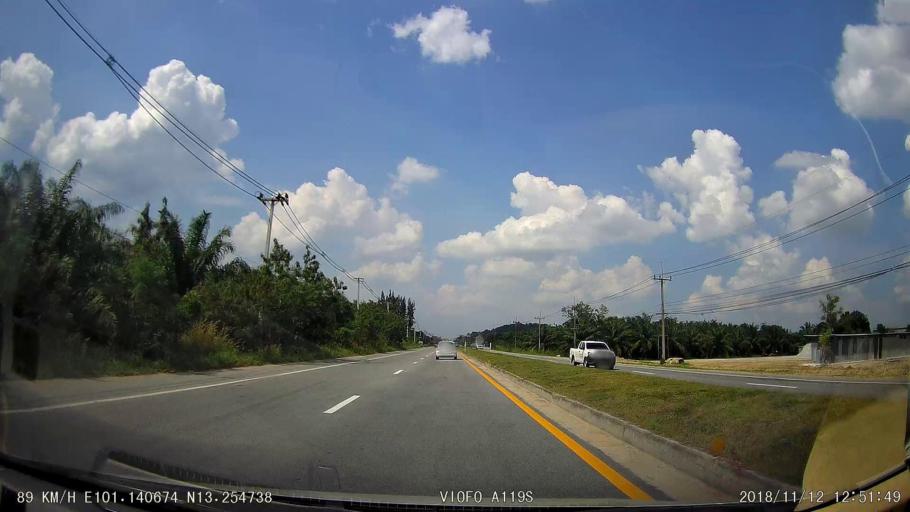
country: TH
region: Chon Buri
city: Ban Bueng
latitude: 13.2550
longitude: 101.1405
